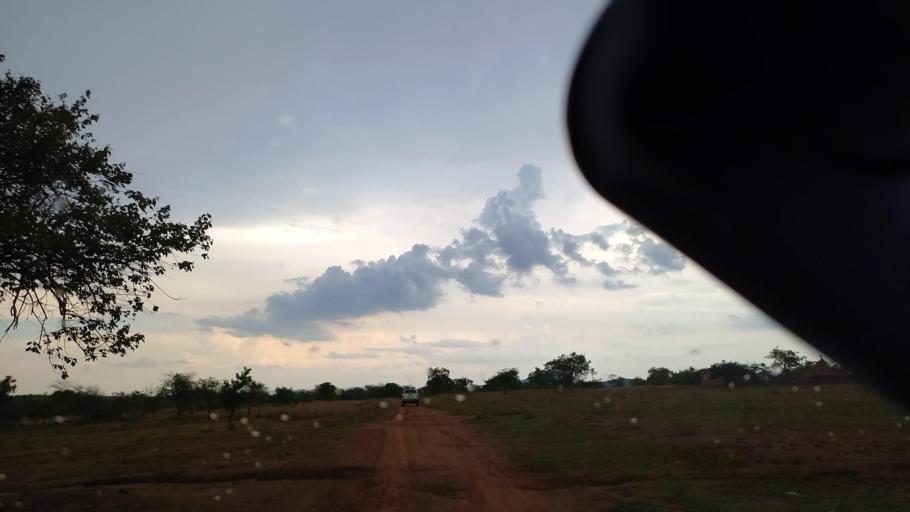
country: ZM
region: Lusaka
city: Kafue
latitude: -15.9759
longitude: 28.2537
